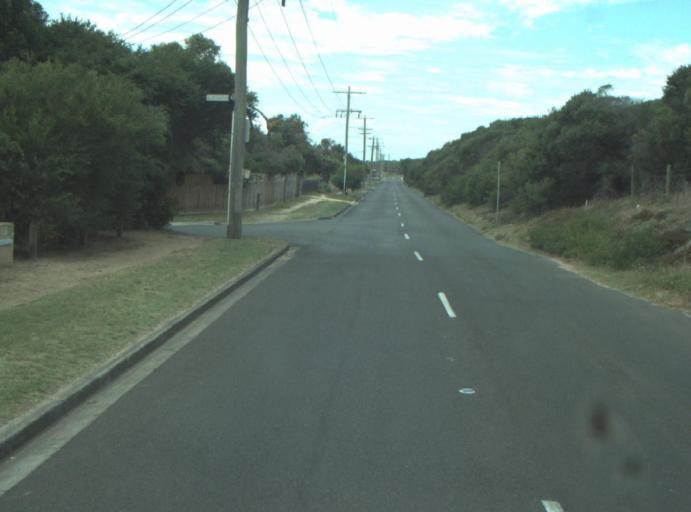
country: AU
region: Victoria
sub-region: Greater Geelong
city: Leopold
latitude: -38.2703
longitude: 144.5413
